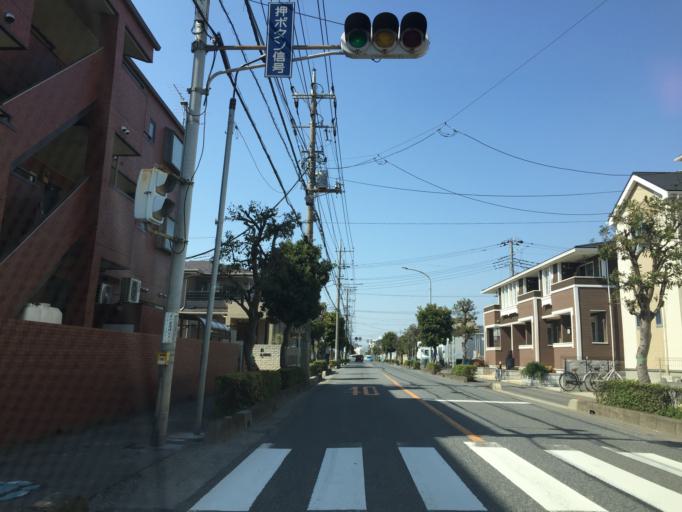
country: JP
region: Saitama
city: Shiki
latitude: 35.8462
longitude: 139.5899
